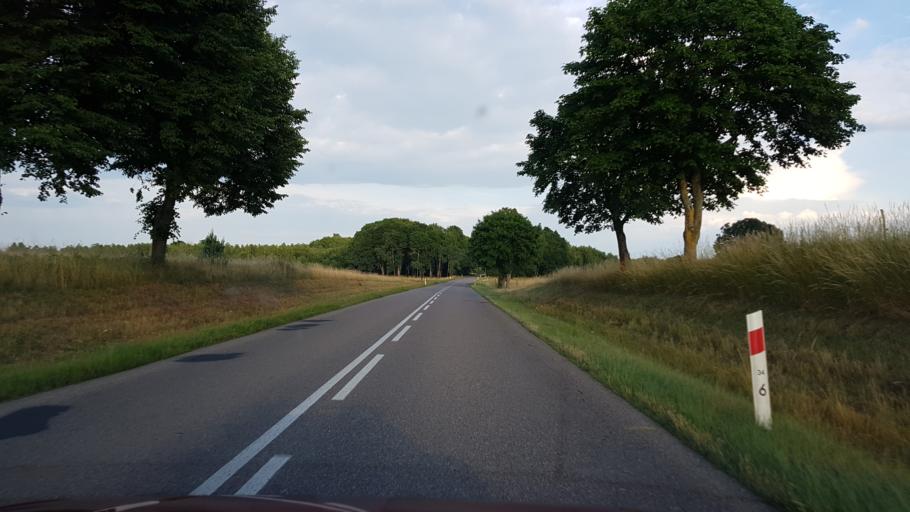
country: PL
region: West Pomeranian Voivodeship
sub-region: Powiat goleniowski
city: Nowogard
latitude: 53.6961
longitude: 15.0603
